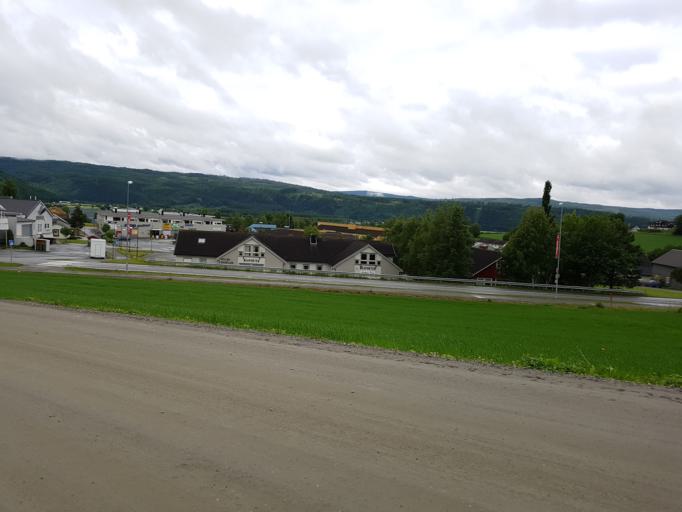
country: NO
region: Sor-Trondelag
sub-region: Selbu
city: Mebonden
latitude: 63.2205
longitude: 11.0407
